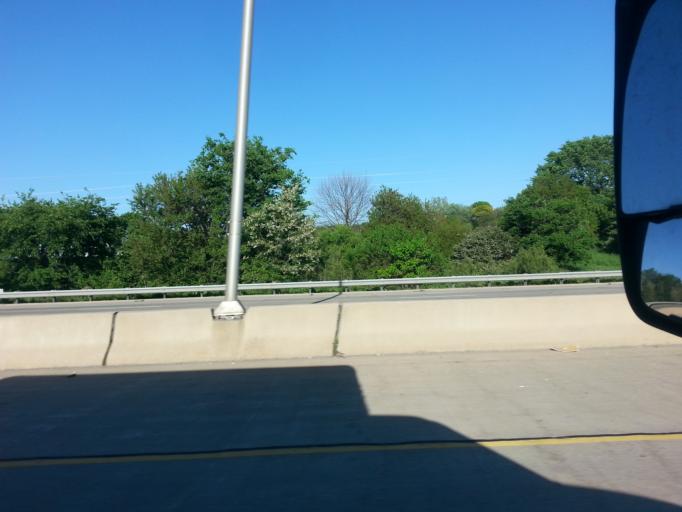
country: US
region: Illinois
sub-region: McLean County
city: Bloomington
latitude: 40.4688
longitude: -89.0313
